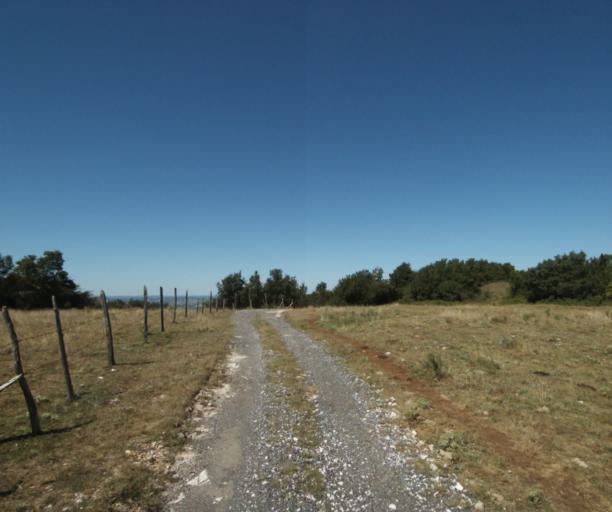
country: FR
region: Midi-Pyrenees
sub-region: Departement du Tarn
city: Soreze
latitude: 43.4466
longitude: 2.0882
